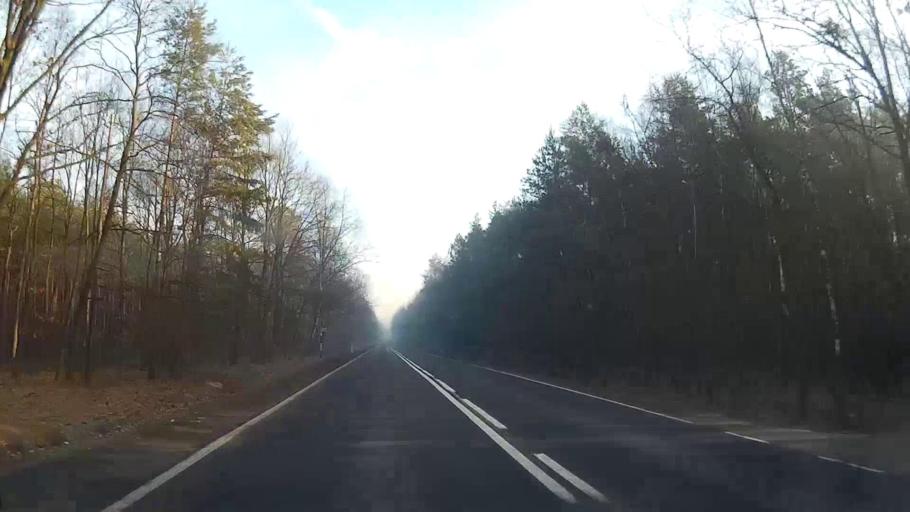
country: PL
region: Lesser Poland Voivodeship
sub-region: Powiat oswiecimski
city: Chelmek
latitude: 50.0803
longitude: 19.2777
